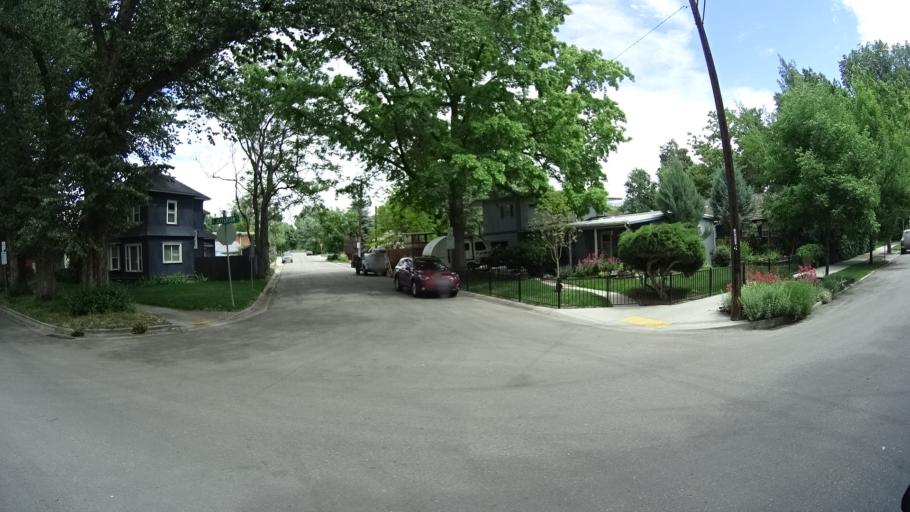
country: US
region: Idaho
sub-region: Ada County
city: Boise
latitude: 43.6117
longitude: -116.1890
